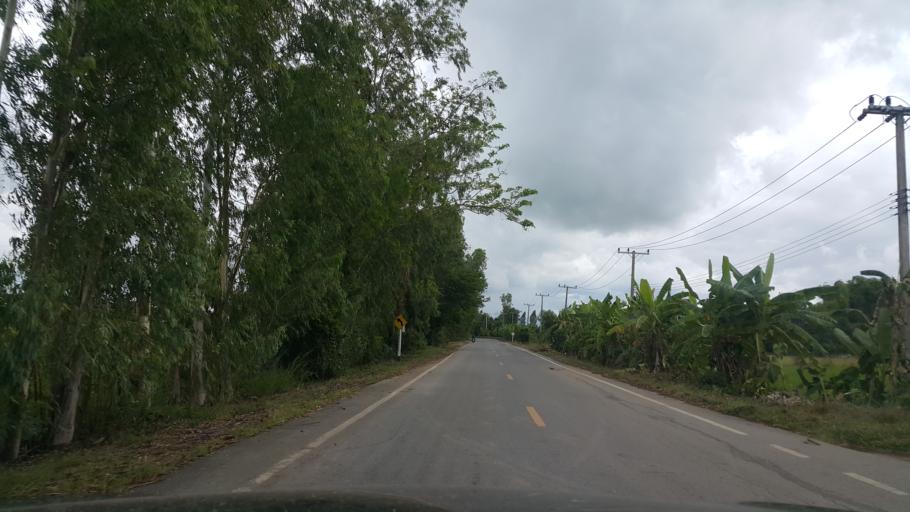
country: TH
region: Sukhothai
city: Kong Krailat
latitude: 16.9241
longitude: 99.8917
